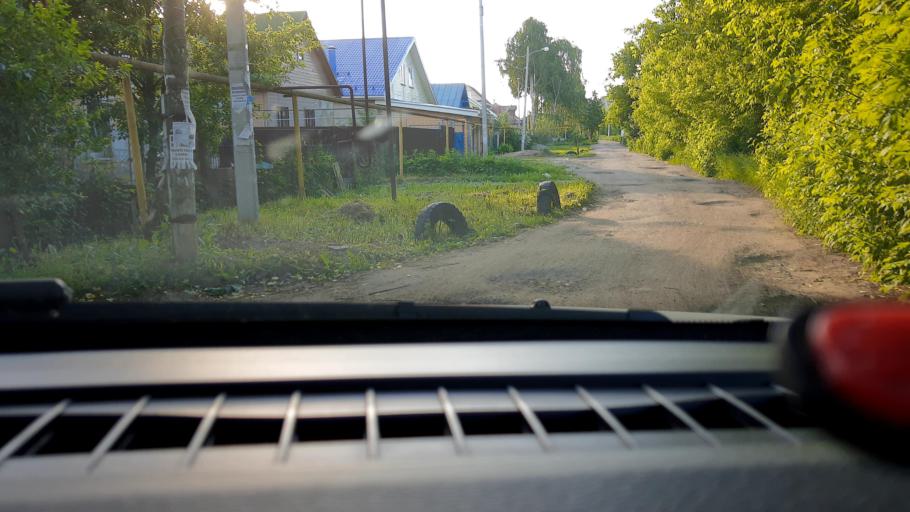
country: RU
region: Nizjnij Novgorod
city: Burevestnik
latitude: 56.2221
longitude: 43.8259
